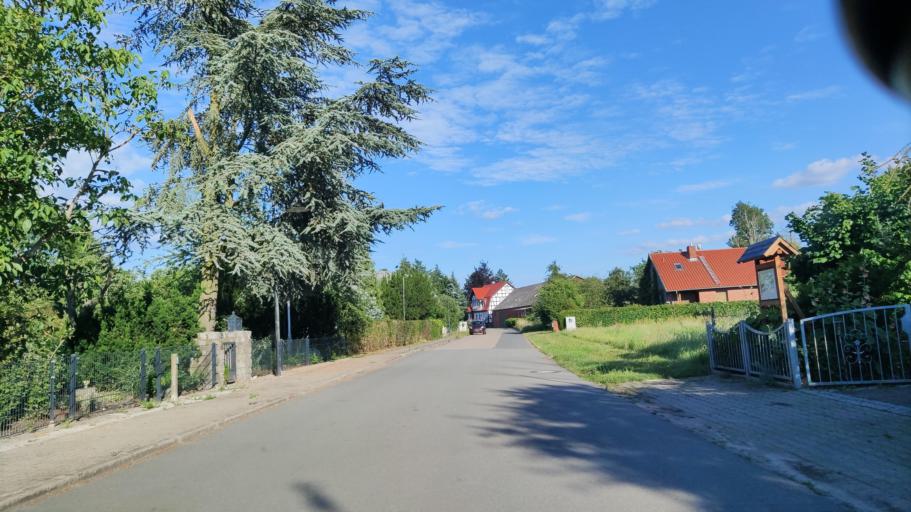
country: DE
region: Brandenburg
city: Lanz
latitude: 53.0387
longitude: 11.5592
